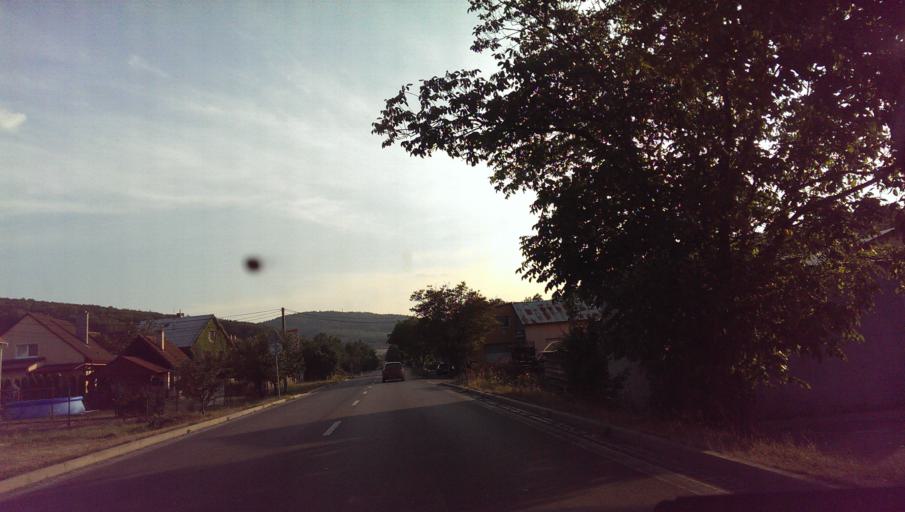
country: CZ
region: Zlin
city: Pozlovice
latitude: 49.1355
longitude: 17.8101
